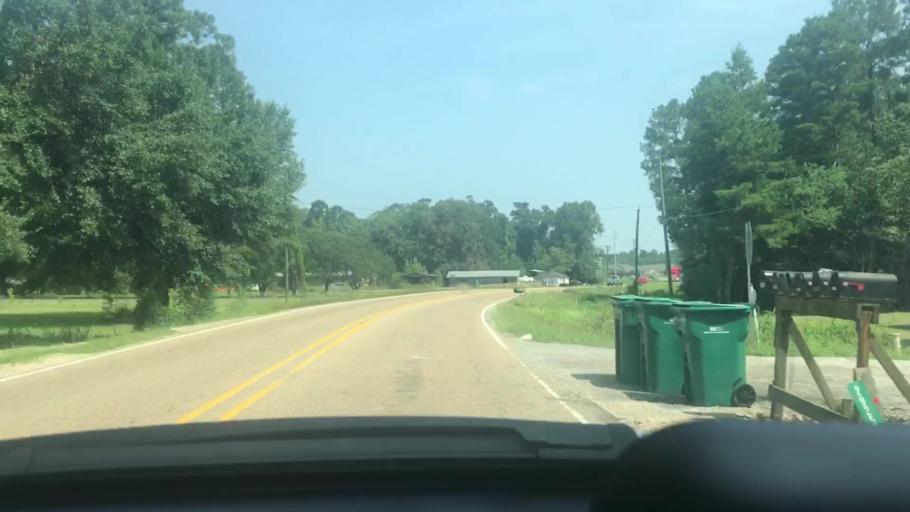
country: US
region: Louisiana
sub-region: Livingston Parish
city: Denham Springs
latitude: 30.4794
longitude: -90.9183
